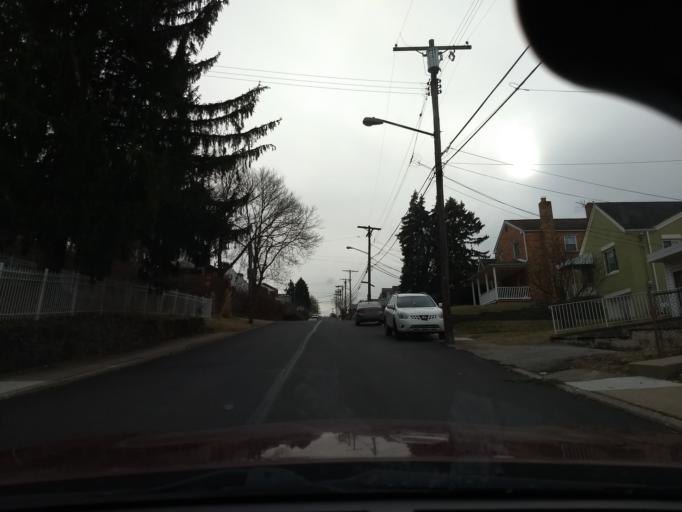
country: US
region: Pennsylvania
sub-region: Allegheny County
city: Homestead
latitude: 40.4218
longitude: -79.9371
